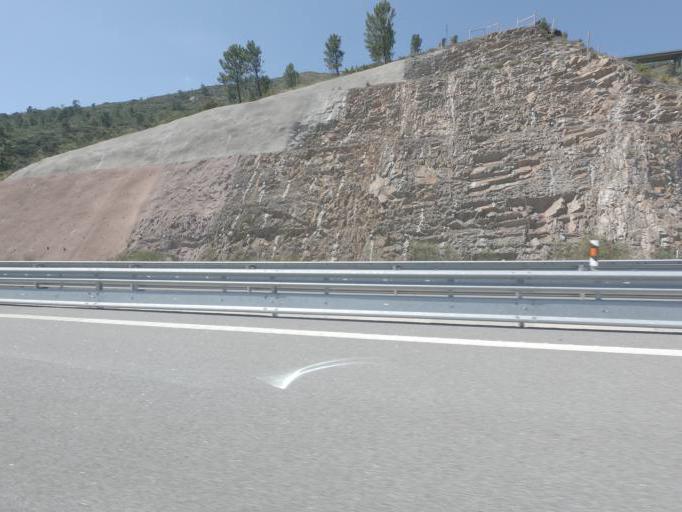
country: PT
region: Porto
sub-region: Baiao
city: Valadares
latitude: 41.2569
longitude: -7.9486
